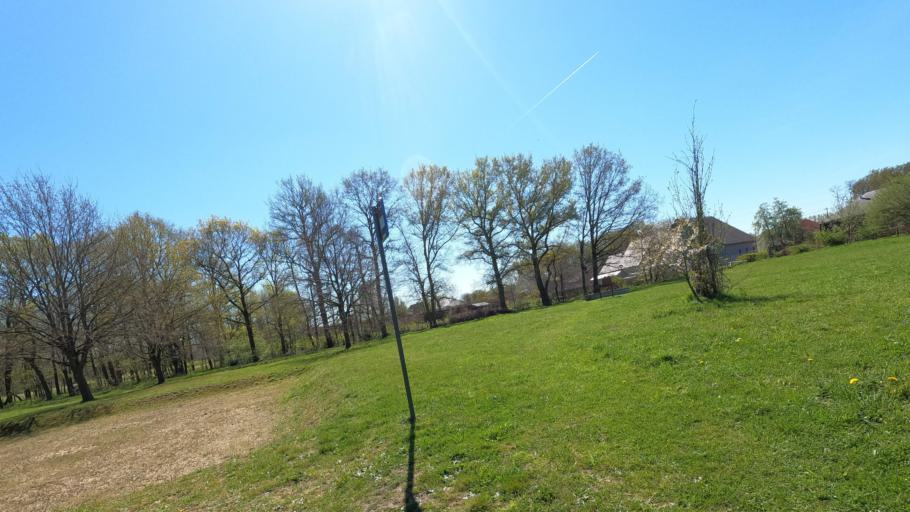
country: BE
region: Flanders
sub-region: Provincie Vlaams-Brabant
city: Haacht
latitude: 50.9832
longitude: 4.6463
